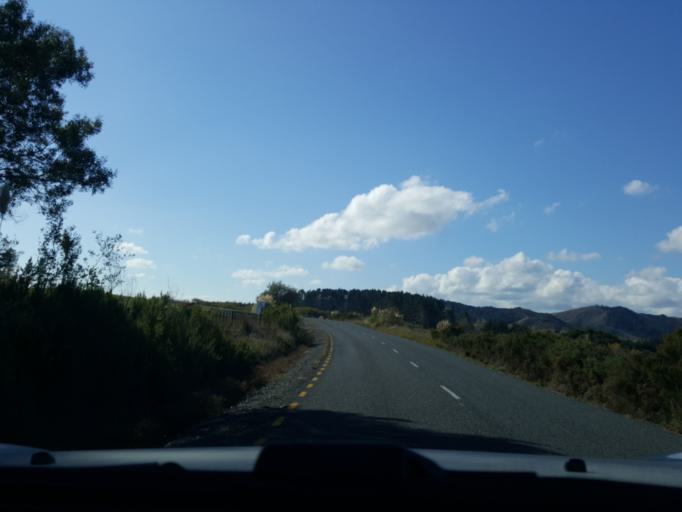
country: NZ
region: Waikato
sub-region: Waikato District
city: Ngaruawahia
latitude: -37.5361
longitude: 175.1770
